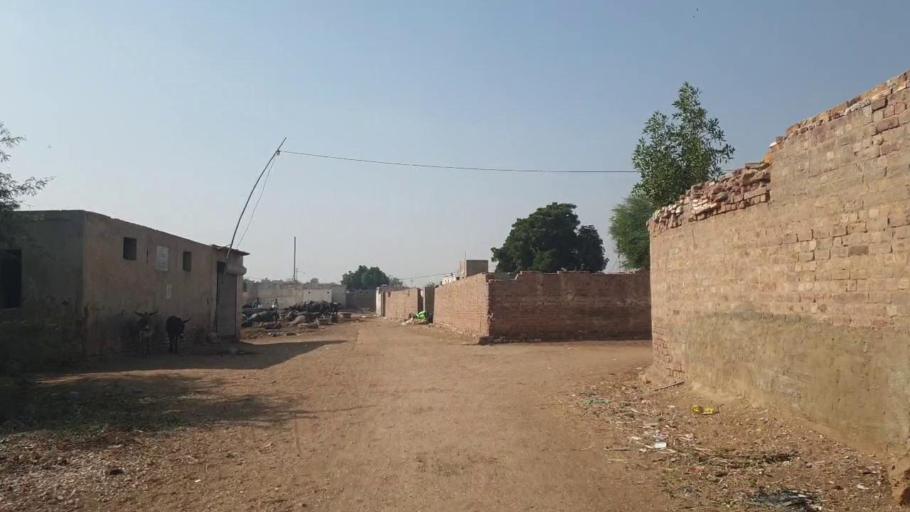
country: PK
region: Sindh
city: Jamshoro
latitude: 25.4501
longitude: 68.2898
